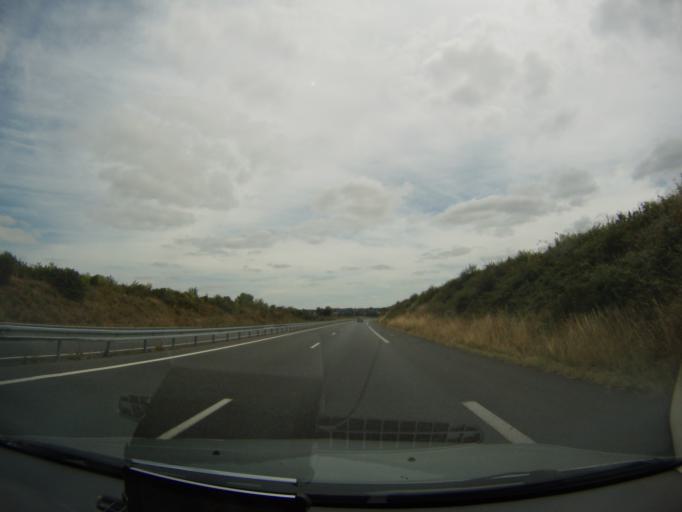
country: FR
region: Poitou-Charentes
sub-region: Departement des Deux-Sevres
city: Saint-Pierre-des-Echaubrognes
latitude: 46.9630
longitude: -0.7899
